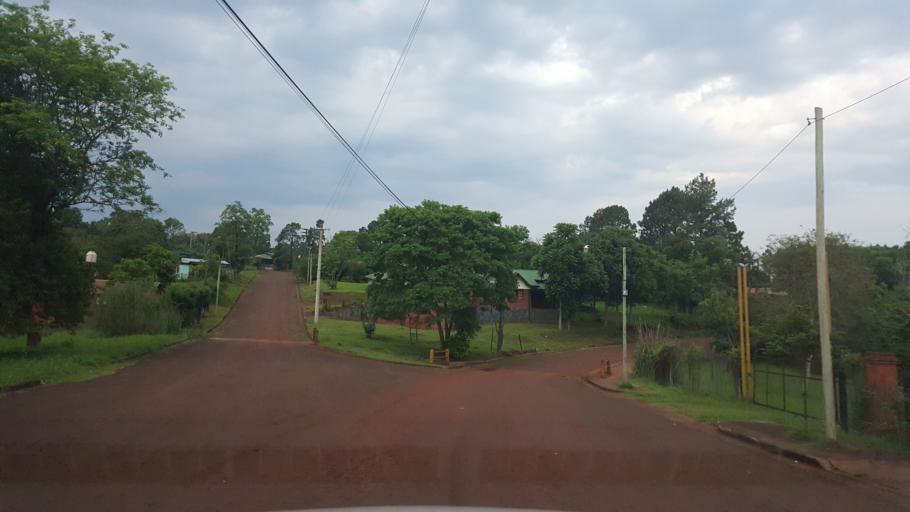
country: AR
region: Misiones
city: Capiovi
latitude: -26.9259
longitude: -55.0620
